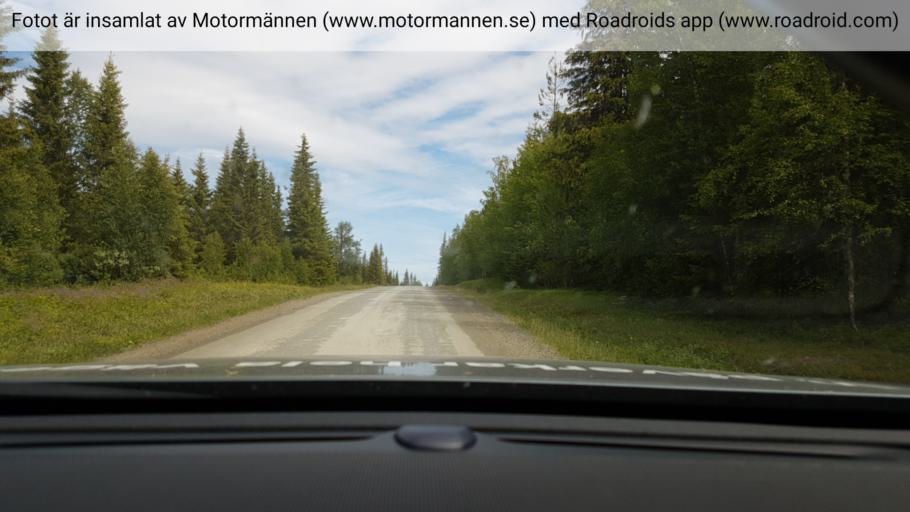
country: SE
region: Vaesterbotten
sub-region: Vilhelmina Kommun
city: Sjoberg
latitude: 65.2008
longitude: 16.1541
